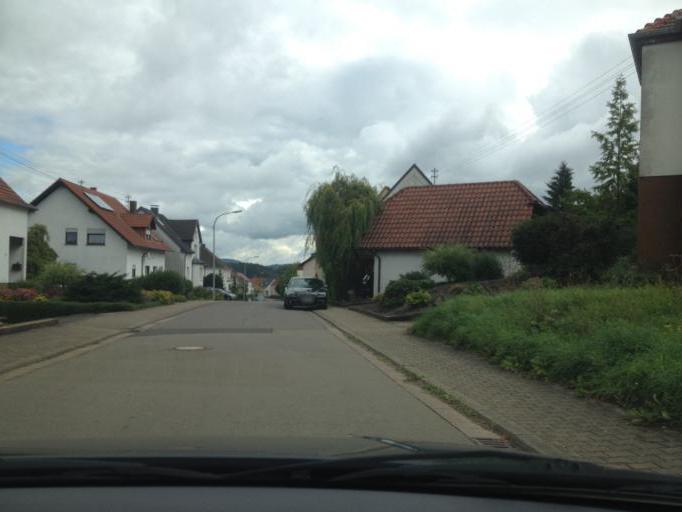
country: DE
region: Saarland
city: Oberthal
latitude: 49.4921
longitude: 7.1083
